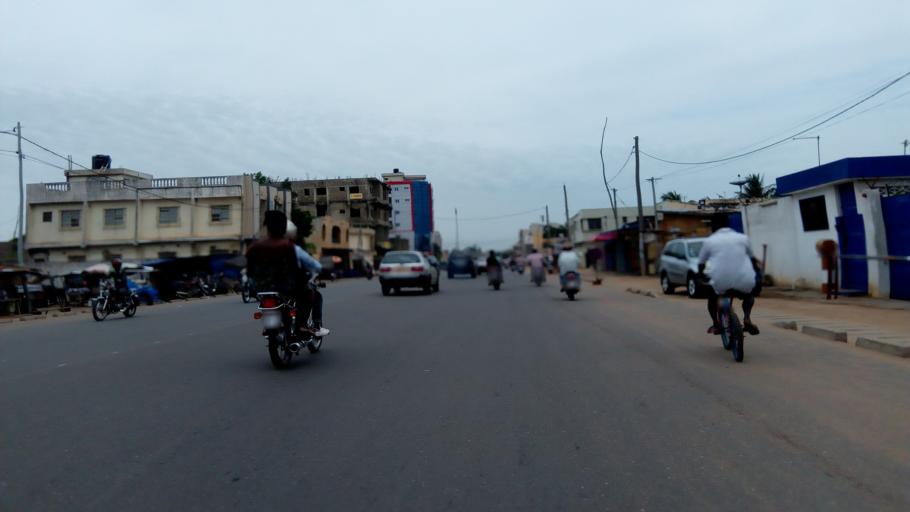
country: TG
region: Maritime
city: Lome
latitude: 6.1521
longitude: 1.2324
